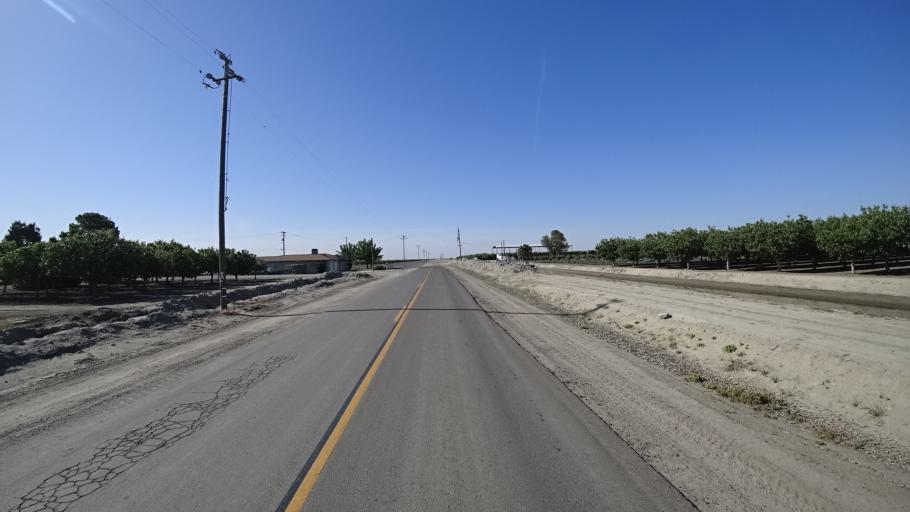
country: US
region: California
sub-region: Kings County
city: Corcoran
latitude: 36.0845
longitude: -119.5899
